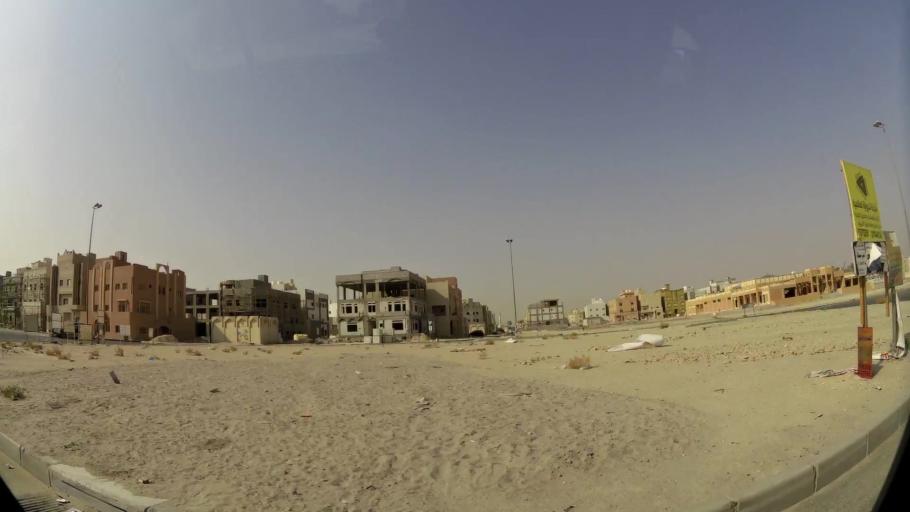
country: KW
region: Muhafazat al Jahra'
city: Al Jahra'
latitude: 29.3472
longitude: 47.7466
